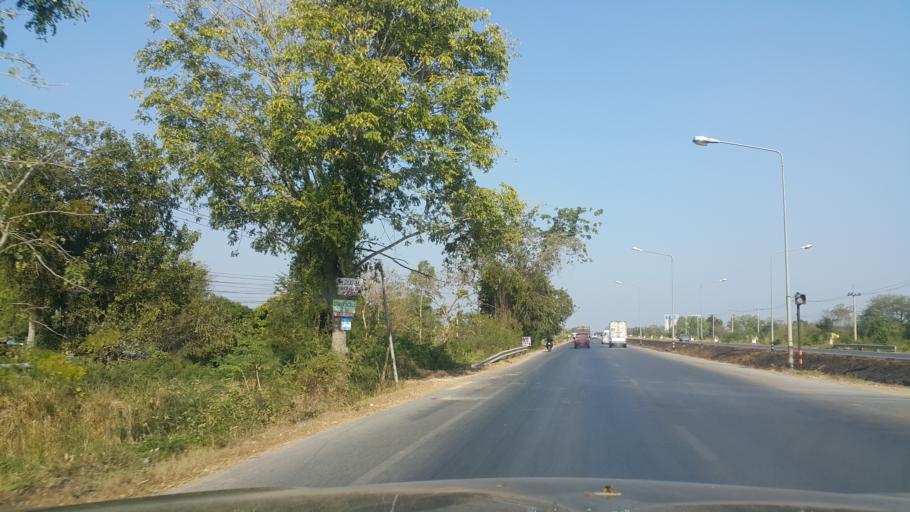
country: TH
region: Khon Kaen
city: Khon Kaen
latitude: 16.4007
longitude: 102.8709
